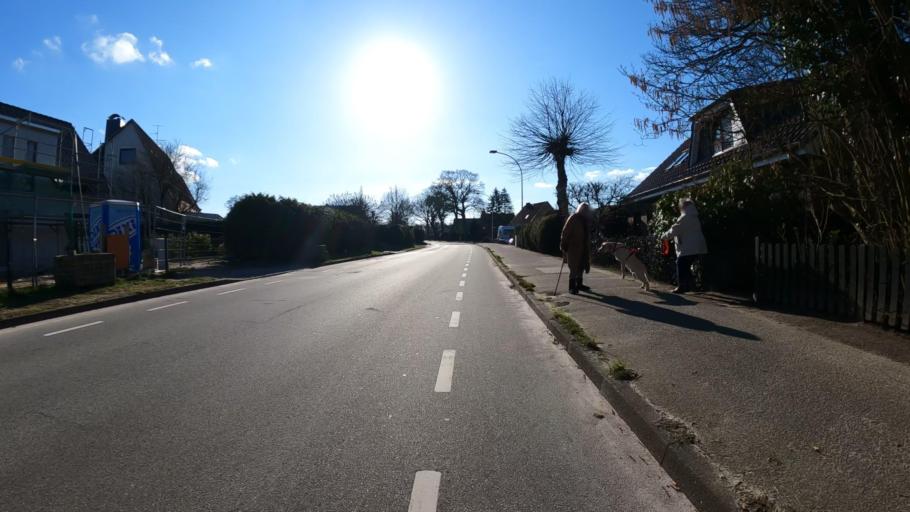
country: DE
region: Schleswig-Holstein
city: Rellingen
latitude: 53.6188
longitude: 9.7971
